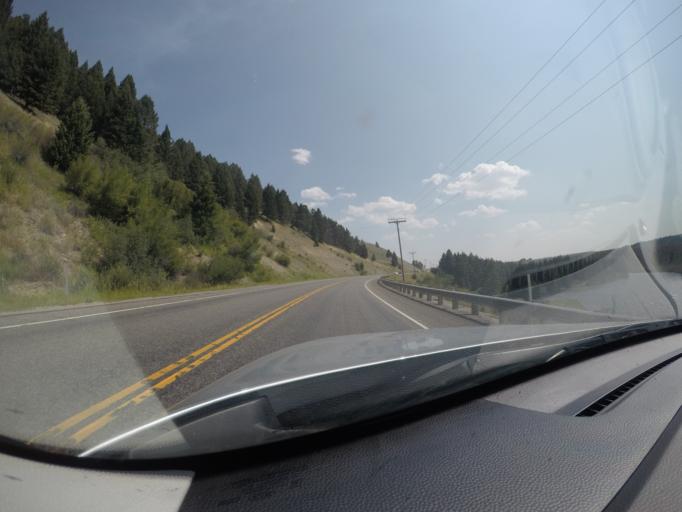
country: US
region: Montana
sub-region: Gallatin County
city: Big Sky
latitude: 44.8624
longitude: -111.5465
